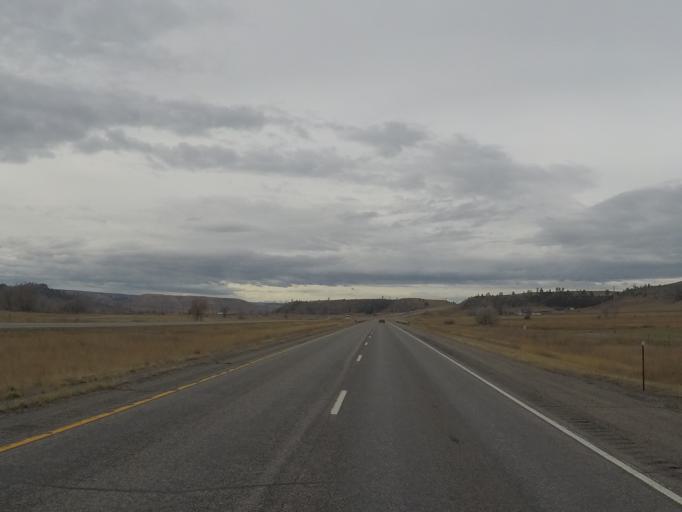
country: US
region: Montana
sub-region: Stillwater County
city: Columbus
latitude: 45.6067
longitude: -109.0284
